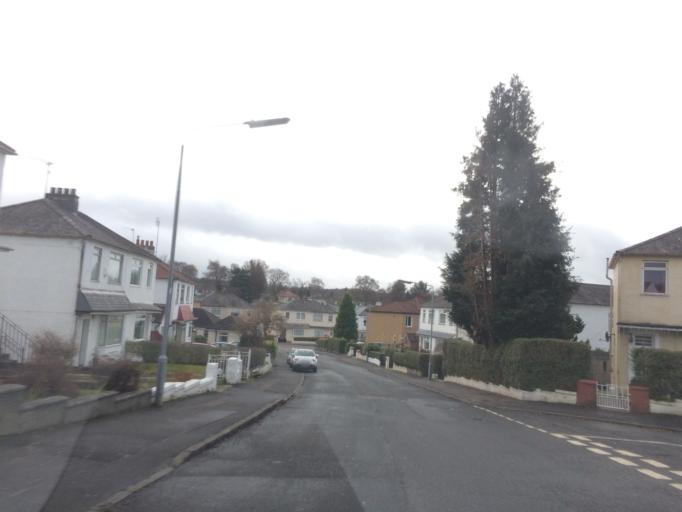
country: GB
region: Scotland
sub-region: East Renfrewshire
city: Giffnock
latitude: 55.8071
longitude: -4.3022
